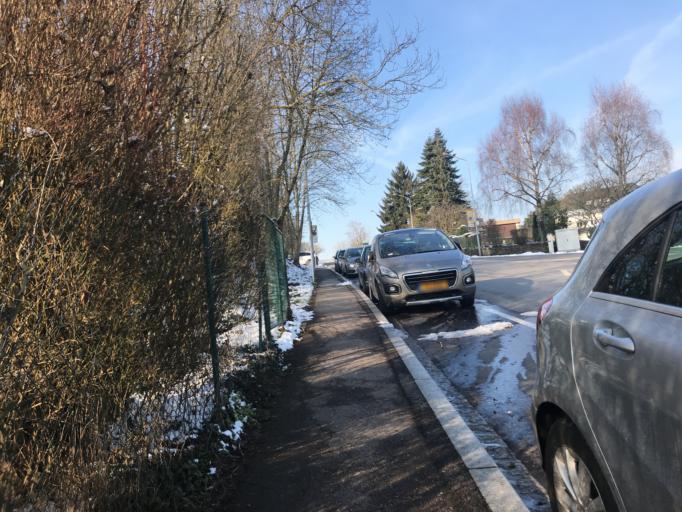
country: LU
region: Luxembourg
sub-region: Canton de Luxembourg
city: Luxembourg
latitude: 49.6038
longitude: 6.1419
